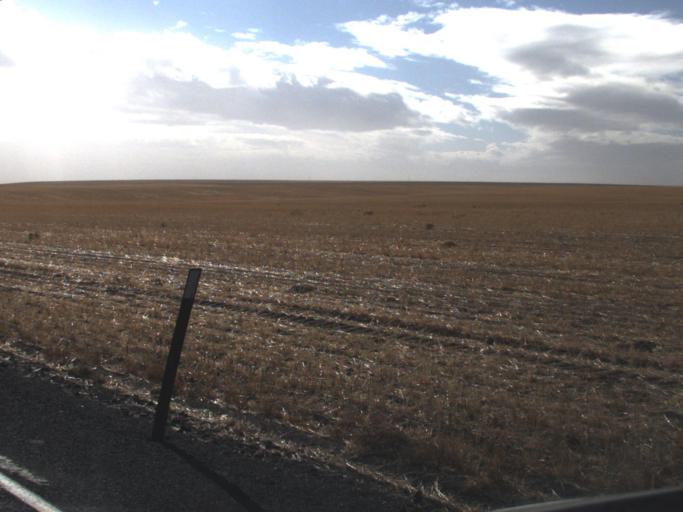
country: US
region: Washington
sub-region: Okanogan County
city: Coulee Dam
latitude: 47.5761
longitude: -118.7859
